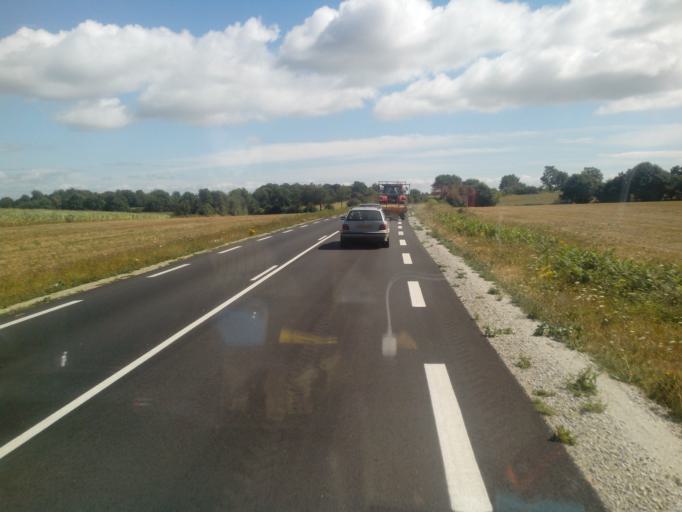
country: FR
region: Brittany
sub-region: Departement du Morbihan
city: Peaule
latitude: 47.6064
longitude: -2.3854
